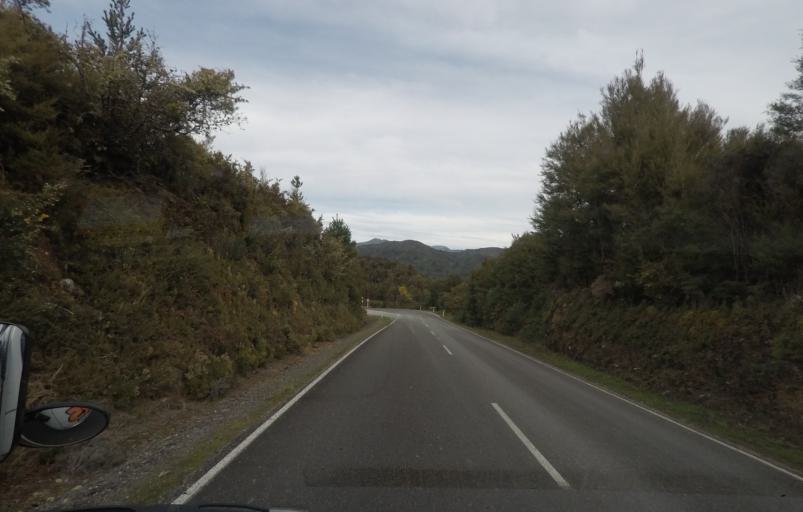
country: NZ
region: Tasman
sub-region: Tasman District
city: Takaka
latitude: -40.8460
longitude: 172.7734
